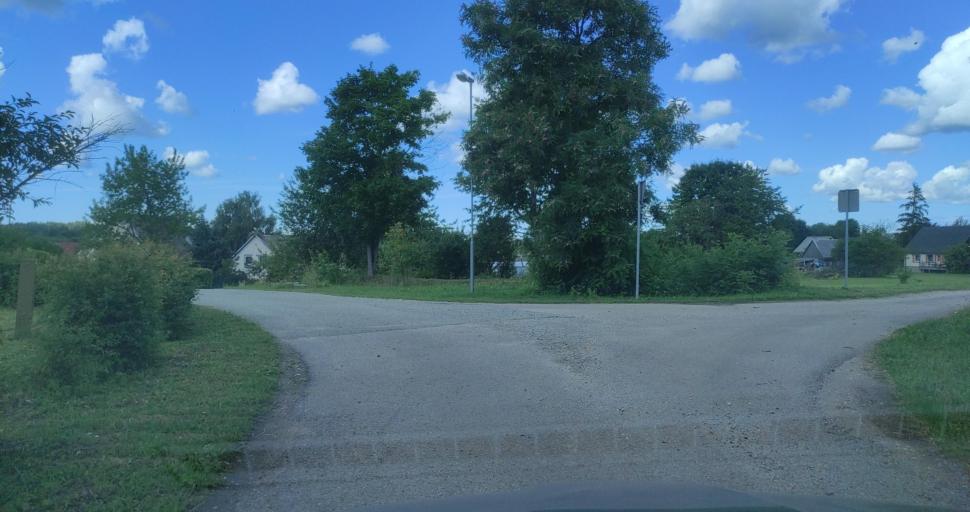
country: LV
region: Alsunga
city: Alsunga
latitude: 57.0206
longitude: 21.6952
